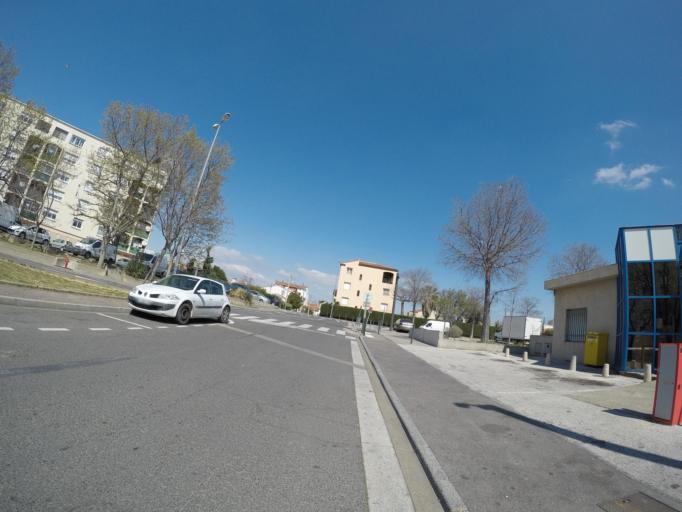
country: FR
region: Languedoc-Roussillon
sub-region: Departement des Pyrenees-Orientales
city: Perpignan
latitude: 42.6940
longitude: 2.9102
